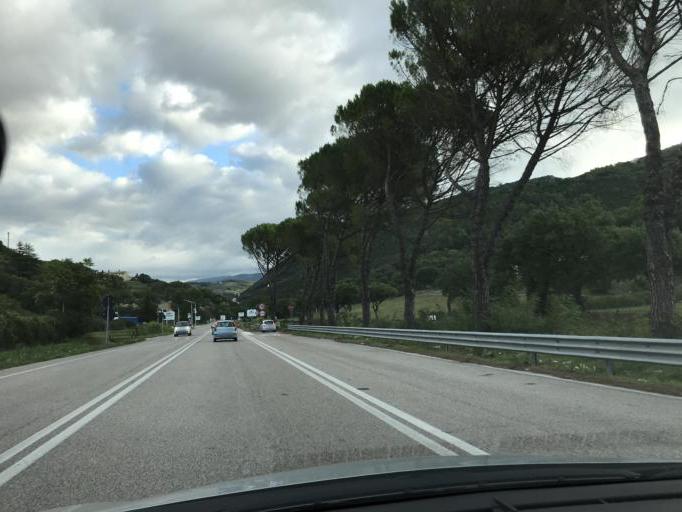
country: IT
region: Umbria
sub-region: Provincia di Perugia
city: Spoleto
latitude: 42.7188
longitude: 12.7277
